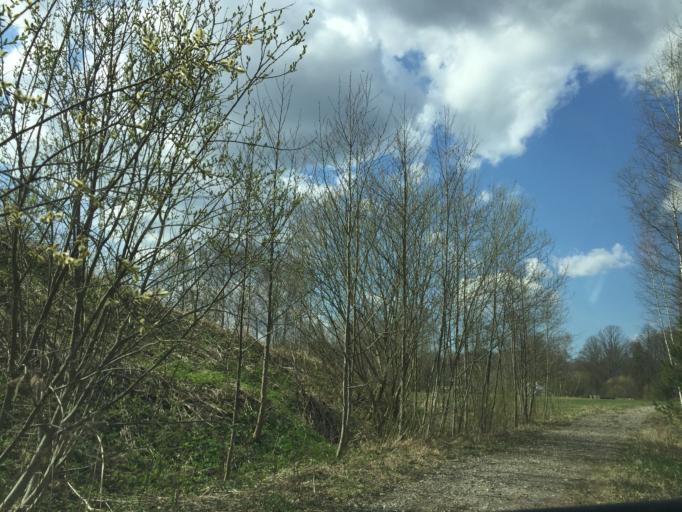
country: LV
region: Skriveri
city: Skriveri
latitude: 56.7461
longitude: 25.1109
